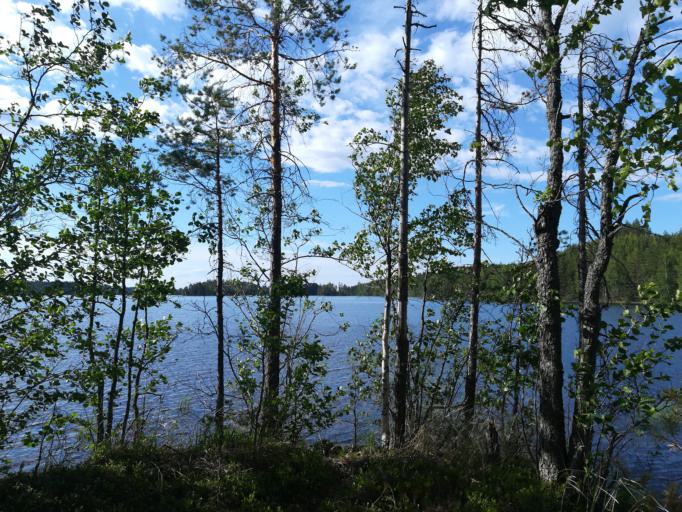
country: FI
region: Southern Savonia
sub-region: Savonlinna
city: Savonlinna
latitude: 61.6451
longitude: 28.7078
